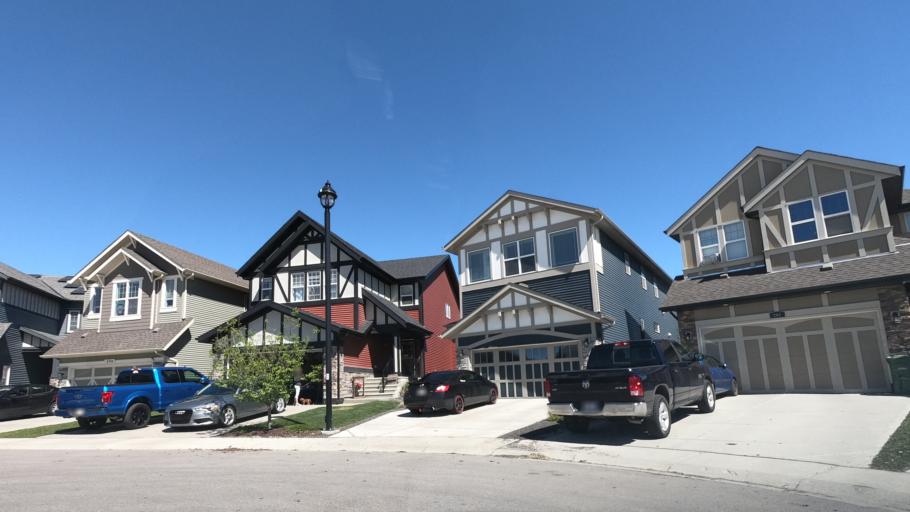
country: CA
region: Alberta
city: Airdrie
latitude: 51.2632
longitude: -113.9860
